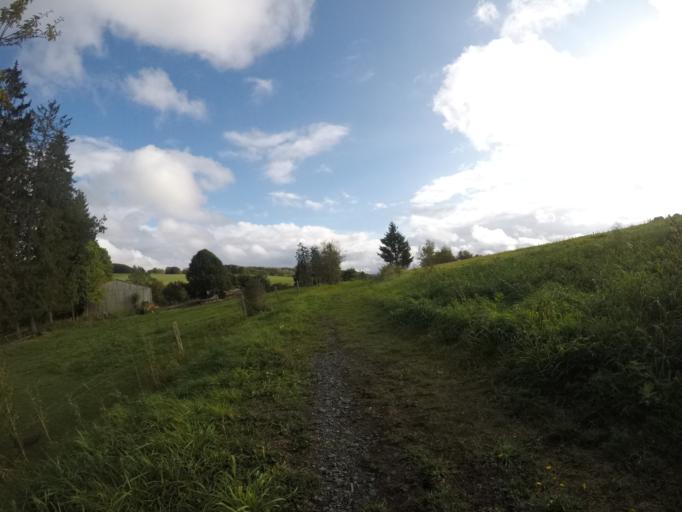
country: BE
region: Wallonia
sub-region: Province du Luxembourg
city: Bastogne
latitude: 49.9495
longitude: 5.6950
